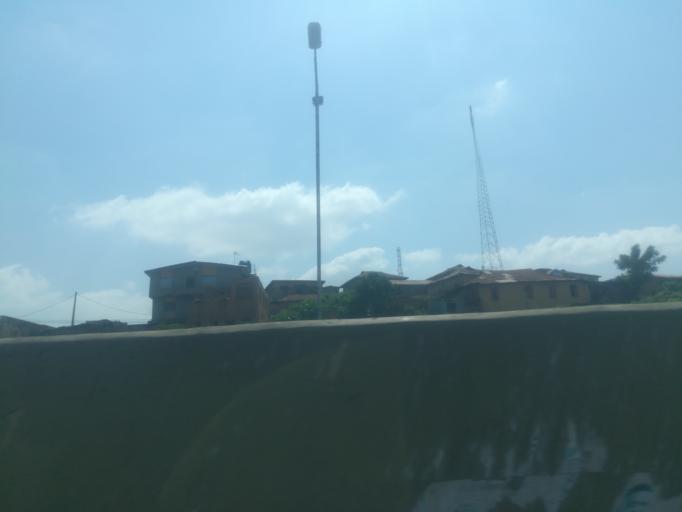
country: NG
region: Ogun
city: Abeokuta
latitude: 7.1569
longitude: 3.3357
